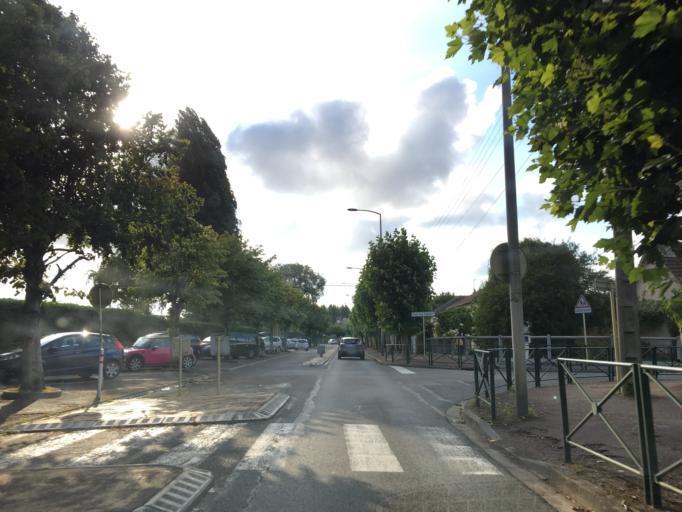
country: FR
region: Lower Normandy
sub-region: Departement du Calvados
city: Cabourg
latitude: 49.2872
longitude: -0.1199
